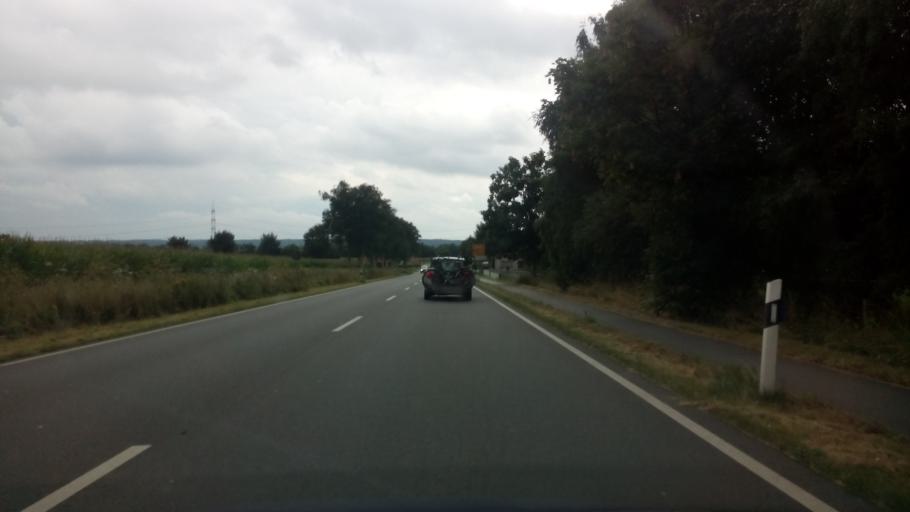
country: DE
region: Lower Saxony
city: Marl
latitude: 52.4877
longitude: 8.3671
